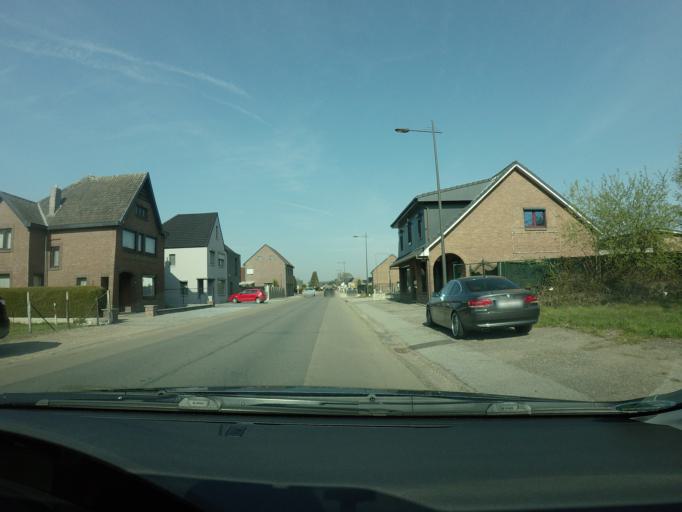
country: BE
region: Flanders
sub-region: Provincie Limburg
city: Maasmechelen
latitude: 50.9463
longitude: 5.6801
